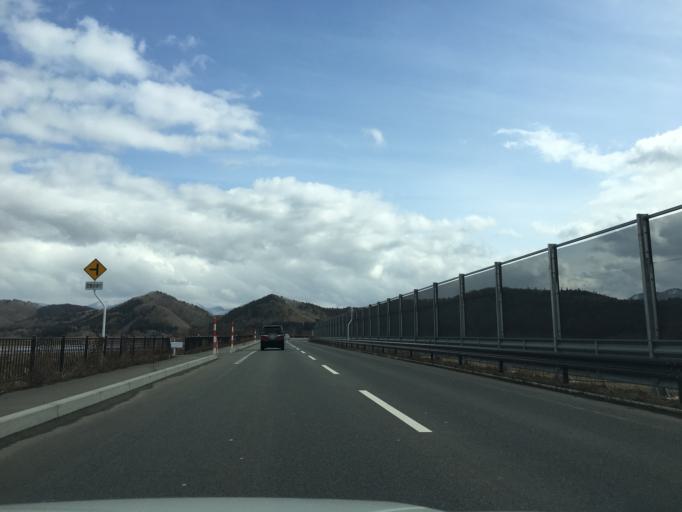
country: JP
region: Akita
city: Hanawa
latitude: 40.2283
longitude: 140.7112
